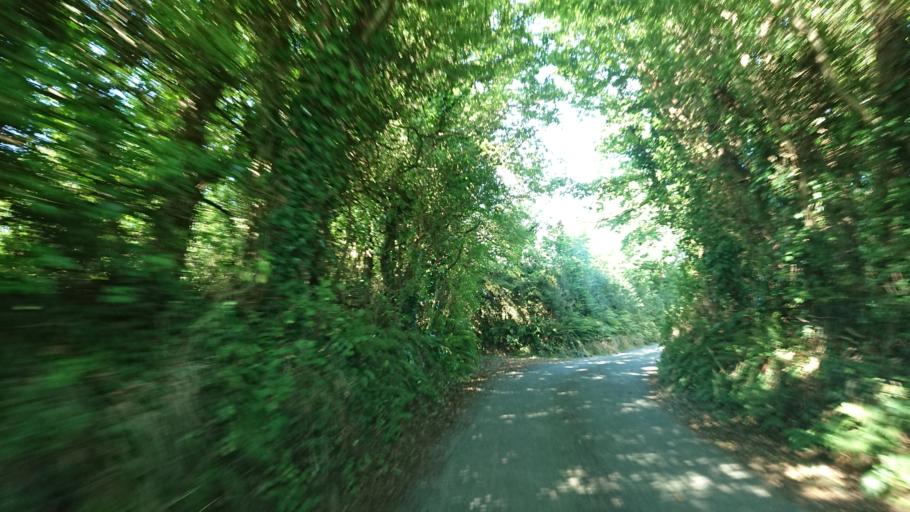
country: IE
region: Munster
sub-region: Waterford
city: Waterford
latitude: 52.2057
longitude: -7.0579
